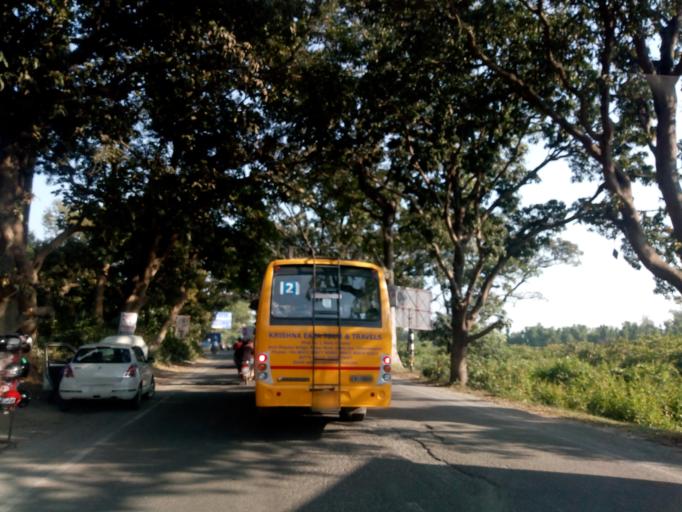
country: IN
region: Uttarakhand
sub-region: Dehradun
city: Vikasnagar
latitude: 30.3479
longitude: 77.8702
